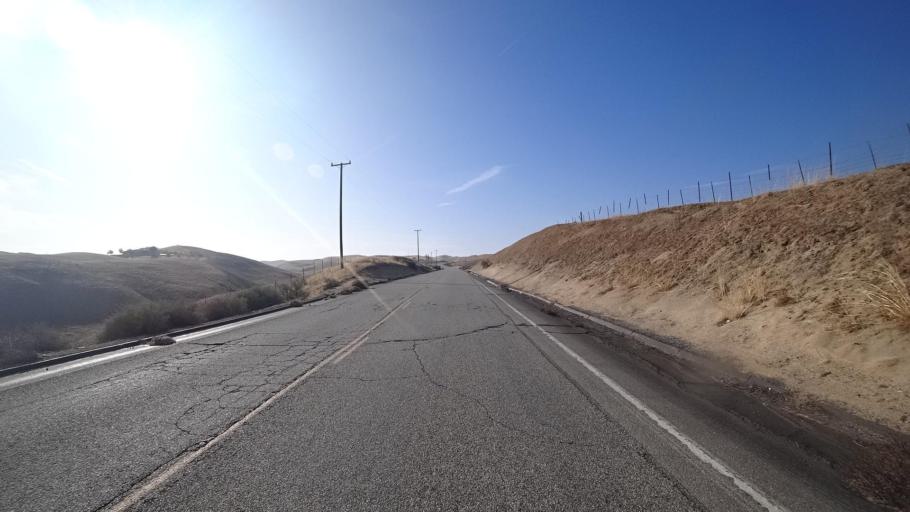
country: US
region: California
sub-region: Kern County
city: Oildale
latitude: 35.5239
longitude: -118.9772
